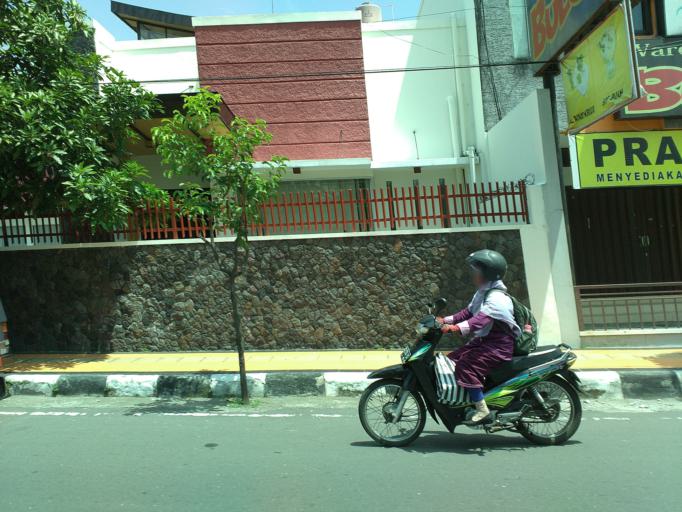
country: ID
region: Central Java
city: Klaten
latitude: -7.7087
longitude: 110.5963
